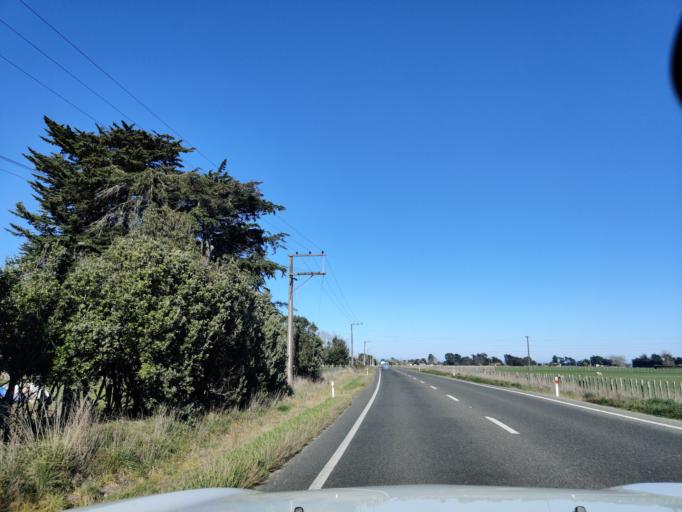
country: NZ
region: Manawatu-Wanganui
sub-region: Palmerston North City
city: Palmerston North
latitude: -40.2550
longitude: 175.5760
